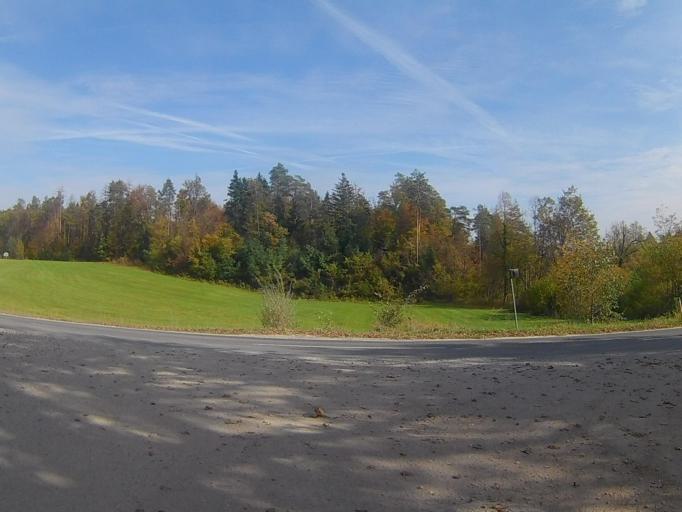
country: SI
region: Selnica ob Dravi
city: Selnica ob Dravi
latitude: 46.5445
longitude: 15.4994
